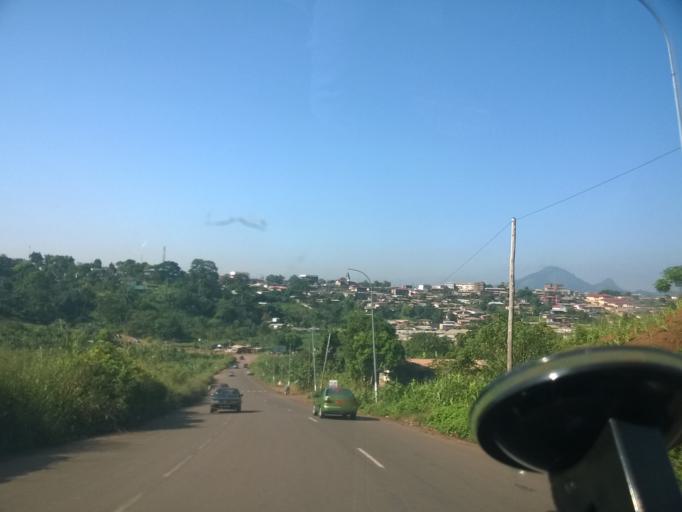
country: CM
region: Centre
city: Yaounde
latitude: 3.8501
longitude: 11.5036
